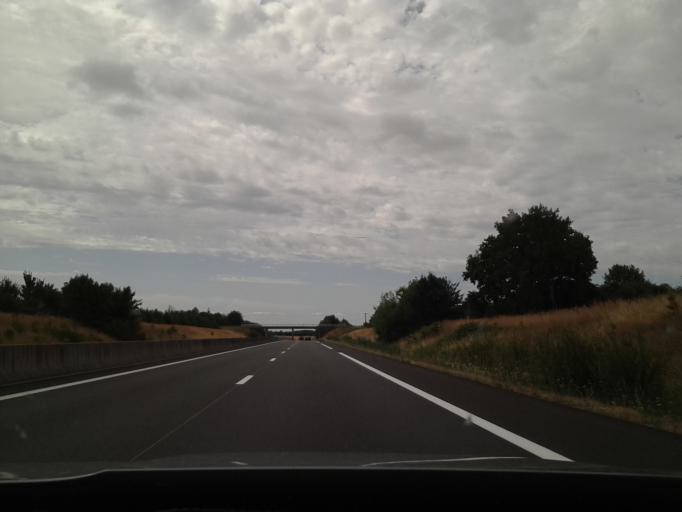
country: FR
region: Pays de la Loire
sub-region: Departement de la Sarthe
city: Beaumont-sur-Sarthe
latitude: 48.2879
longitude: 0.1549
